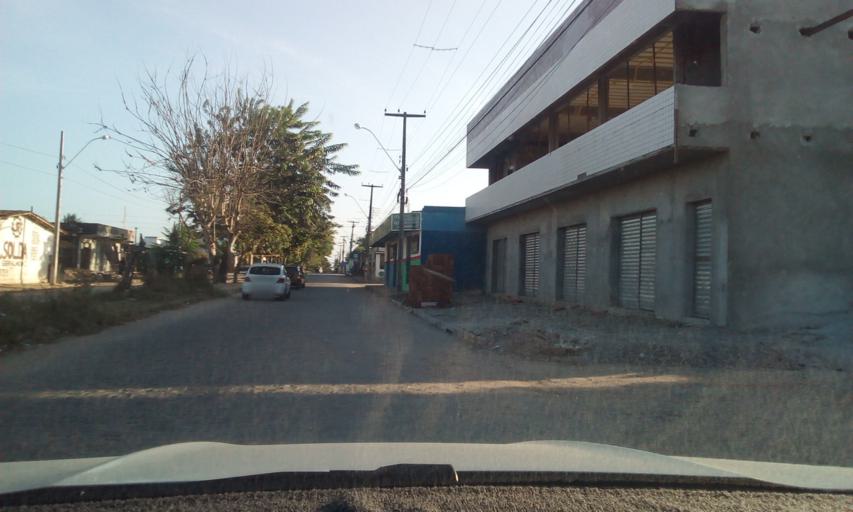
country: BR
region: Paraiba
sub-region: Bayeux
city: Bayeux
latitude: -7.1792
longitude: -34.9331
